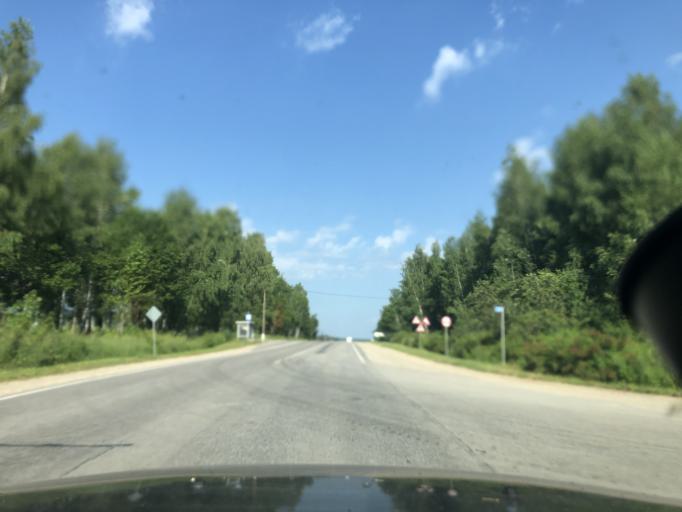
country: RU
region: Tula
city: Dubna
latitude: 54.1464
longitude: 36.9787
